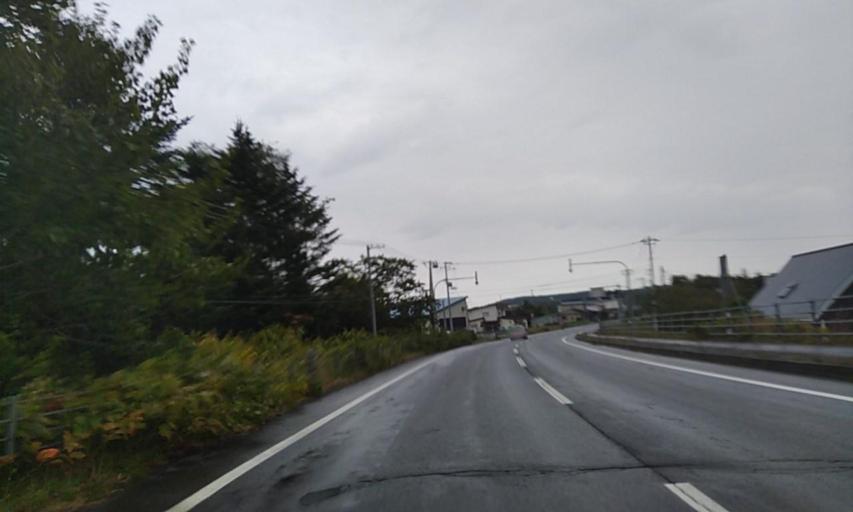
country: JP
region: Hokkaido
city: Mombetsu
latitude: 44.4751
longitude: 143.1196
